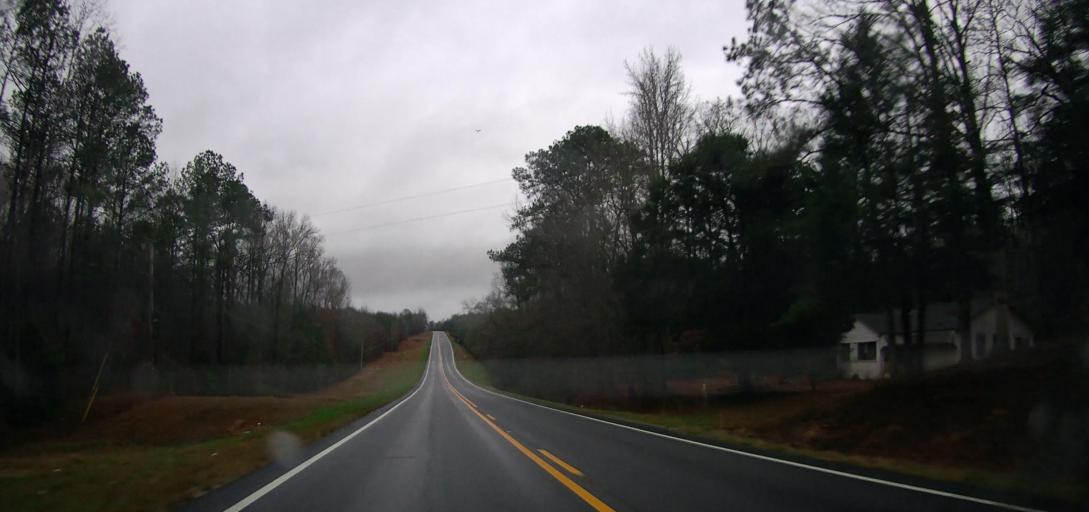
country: US
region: Alabama
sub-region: Bibb County
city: Centreville
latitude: 32.8241
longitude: -86.9449
